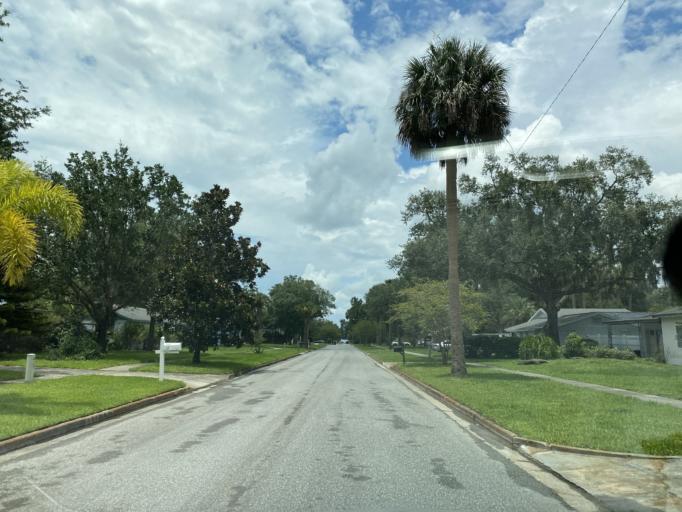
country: US
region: Florida
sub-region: Seminole County
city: Sanford
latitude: 28.8072
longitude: -81.2515
